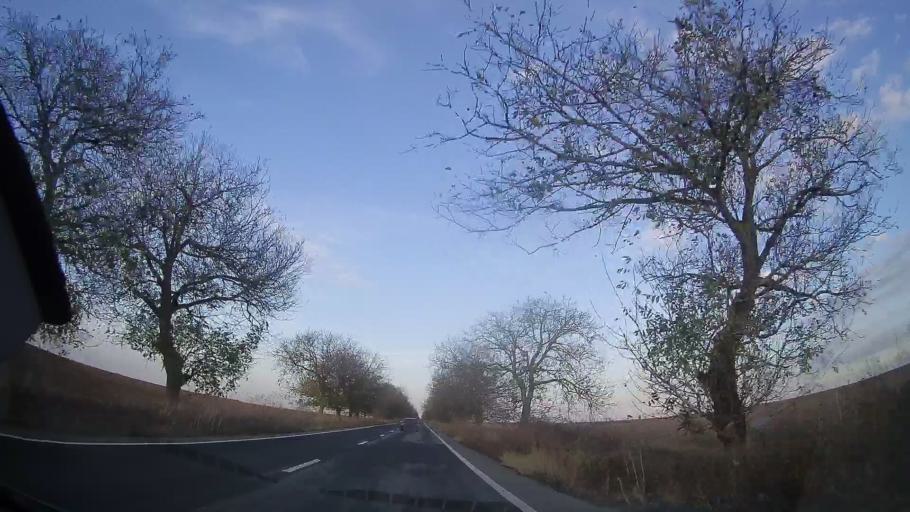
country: RO
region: Constanta
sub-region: Comuna Chirnogeni
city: Chirnogeni
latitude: 43.8651
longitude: 28.2651
